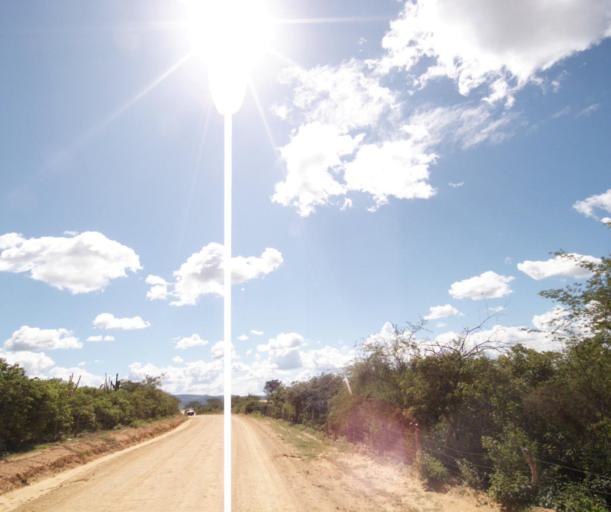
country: BR
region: Bahia
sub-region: Pocoes
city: Pocoes
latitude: -14.2519
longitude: -40.7091
